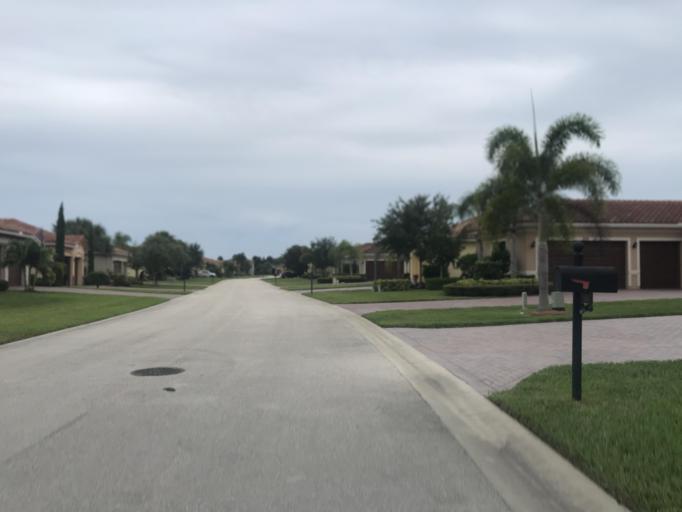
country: US
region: Florida
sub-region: Indian River County
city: Winter Beach
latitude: 27.6965
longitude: -80.4375
